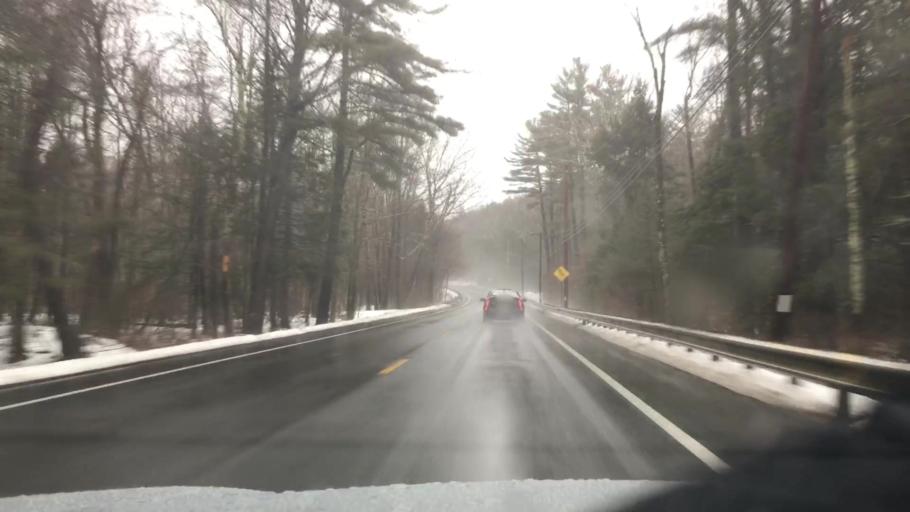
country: US
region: Massachusetts
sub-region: Franklin County
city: Wendell
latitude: 42.4940
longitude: -72.3399
